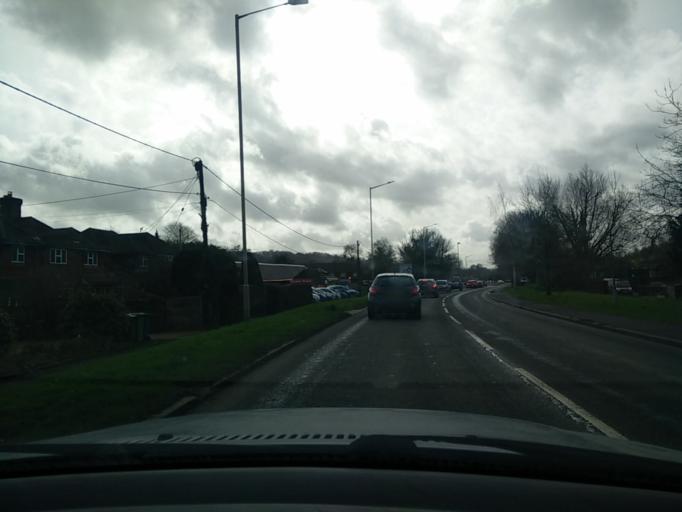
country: GB
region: England
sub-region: Buckinghamshire
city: High Wycombe
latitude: 51.6613
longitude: -0.7515
